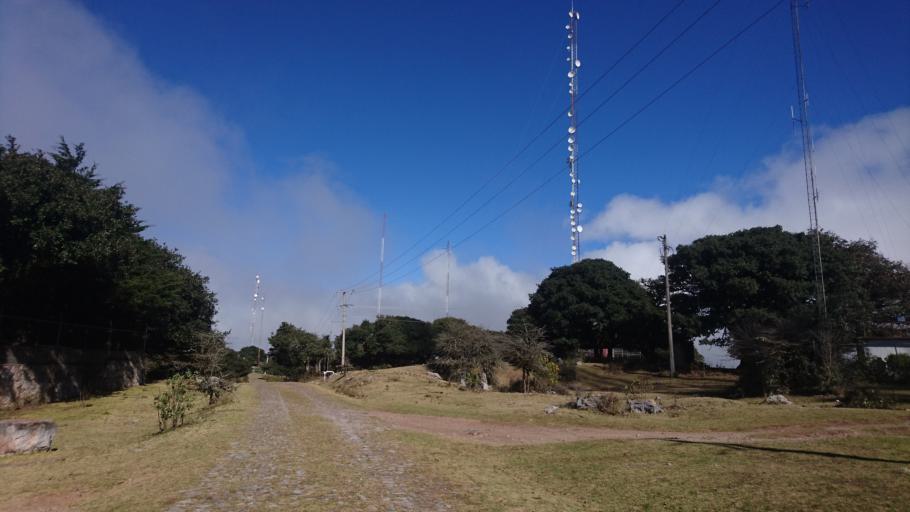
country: MX
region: San Luis Potosi
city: Zaragoza
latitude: 22.0657
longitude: -100.6488
